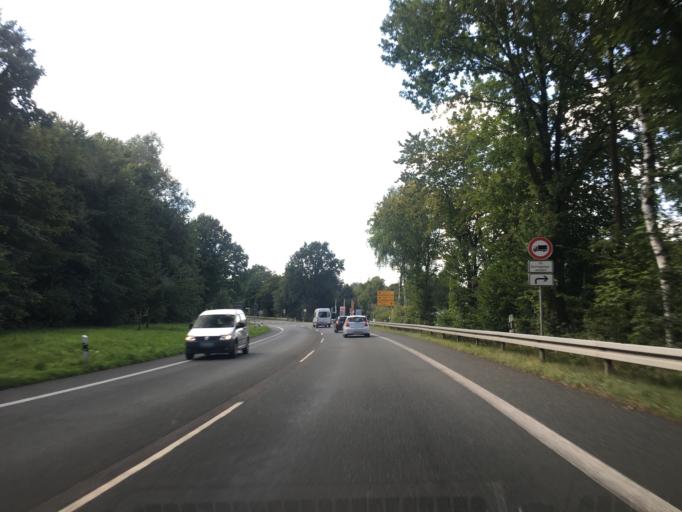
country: DE
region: North Rhine-Westphalia
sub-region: Regierungsbezirk Detmold
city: Dorentrup
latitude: 51.9867
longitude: 8.9998
